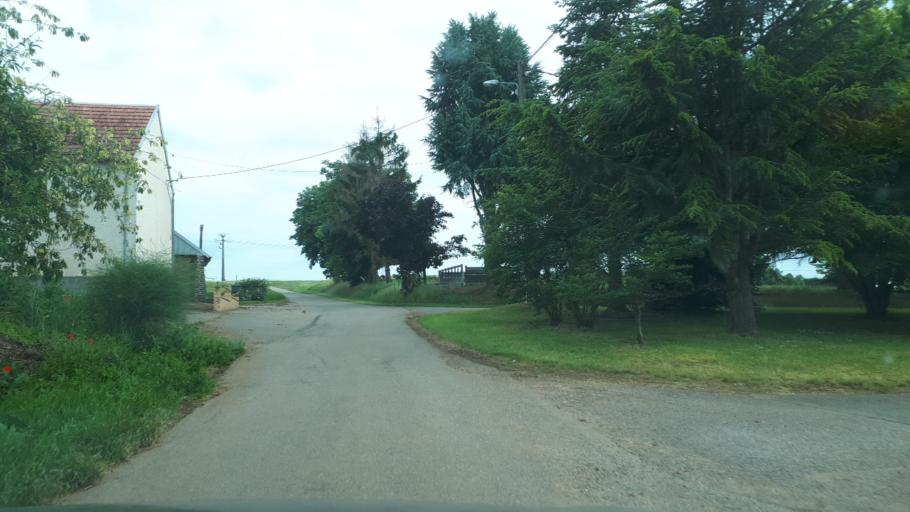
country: FR
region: Centre
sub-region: Departement du Cher
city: Sancerre
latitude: 47.3180
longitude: 2.7401
